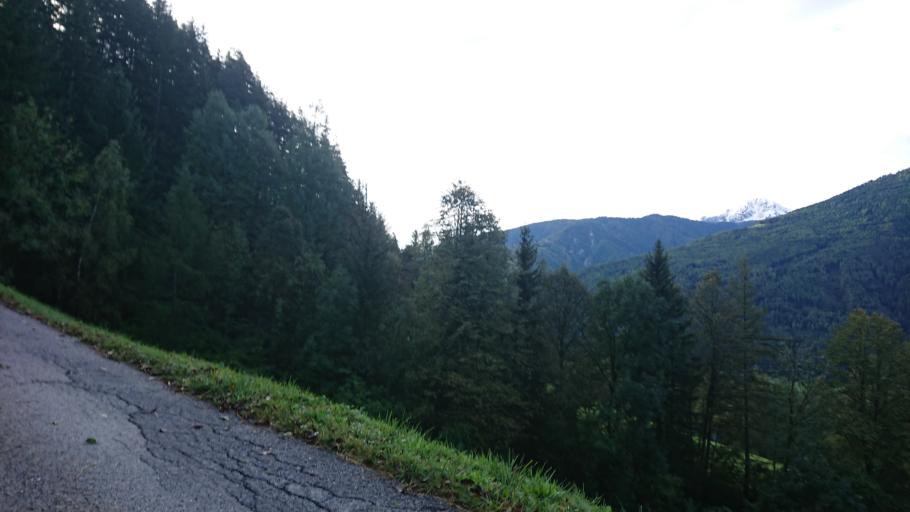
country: IT
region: Trentino-Alto Adige
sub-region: Bolzano
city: Campo di Trens
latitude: 46.8790
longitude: 11.4883
